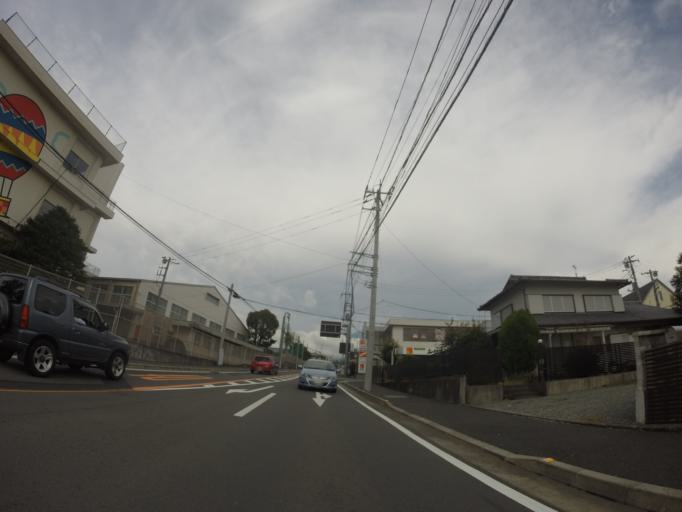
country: JP
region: Shizuoka
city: Fuji
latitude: 35.2113
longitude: 138.6866
